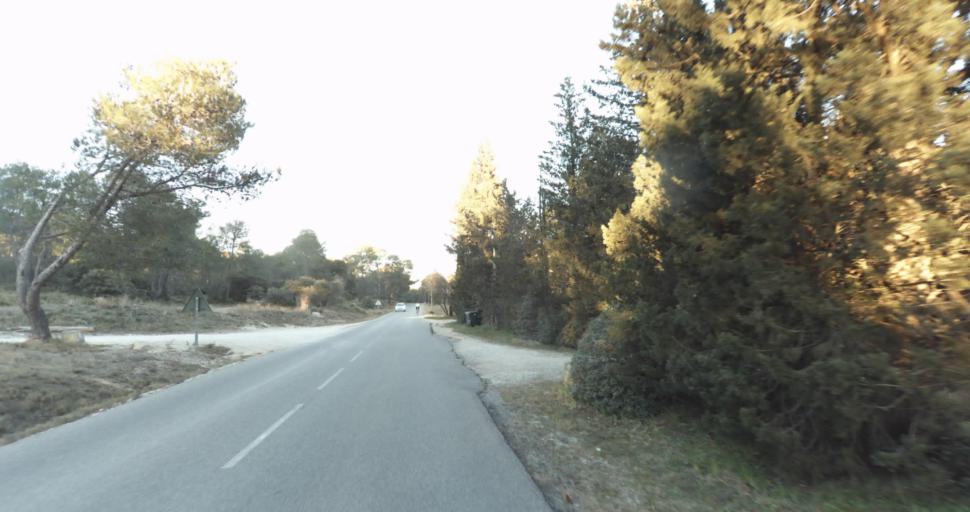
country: FR
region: Provence-Alpes-Cote d'Azur
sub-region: Departement des Bouches-du-Rhone
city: Barbentane
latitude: 43.8733
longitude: 4.7305
